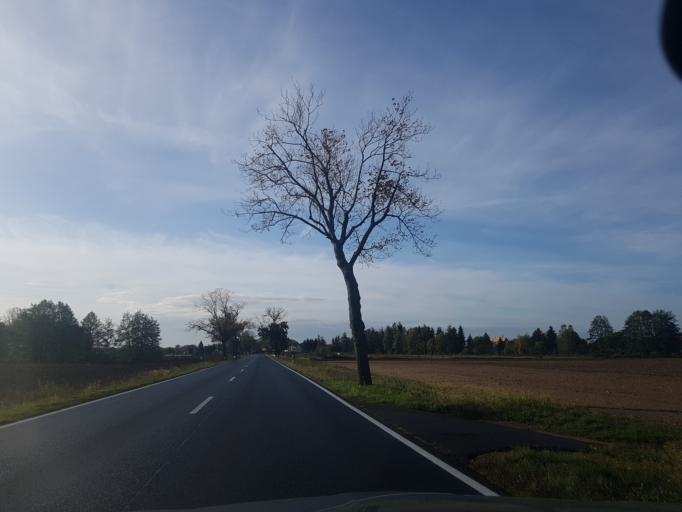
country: DE
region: Saxony
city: Arzberg
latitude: 51.6193
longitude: 13.1465
